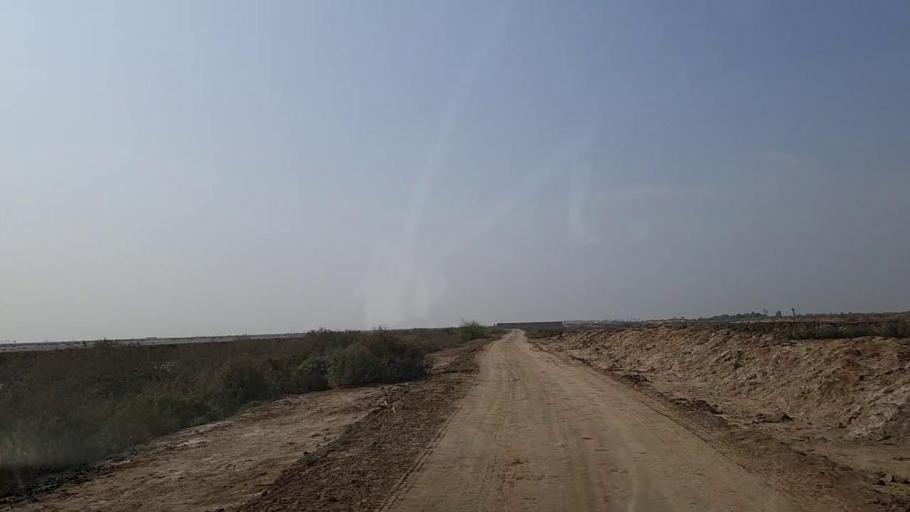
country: PK
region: Sindh
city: Gharo
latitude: 24.6737
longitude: 67.7154
